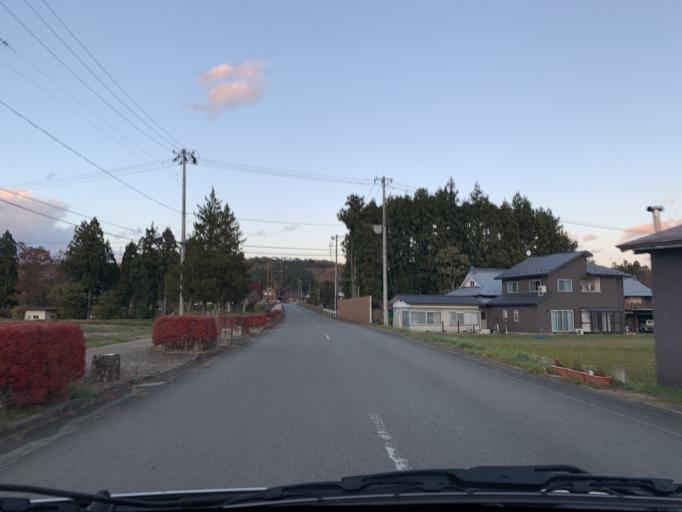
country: JP
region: Iwate
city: Ichinoseki
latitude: 39.0155
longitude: 141.0893
